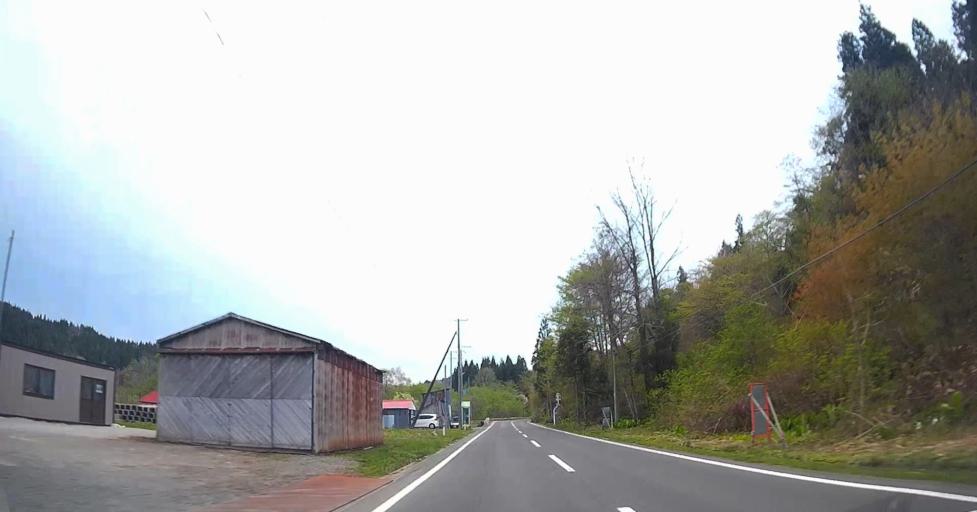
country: JP
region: Aomori
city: Goshogawara
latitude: 41.1293
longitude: 140.5198
